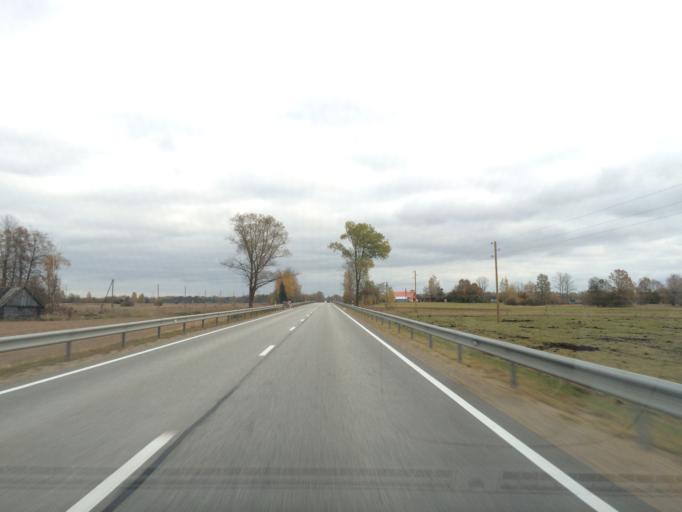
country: LV
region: Livani
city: Livani
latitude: 56.5344
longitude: 26.3142
